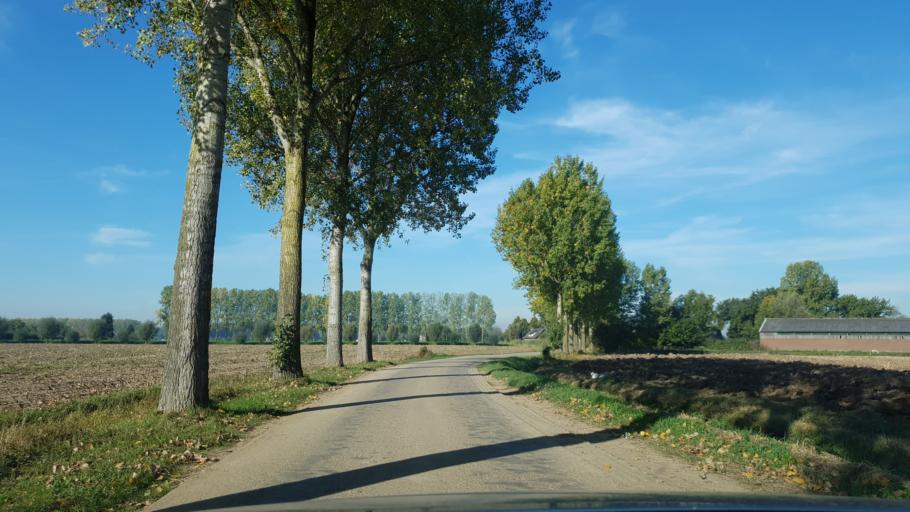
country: NL
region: Gelderland
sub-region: Gemeente Overbetuwe
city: Andelst
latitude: 51.8693
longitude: 5.7097
